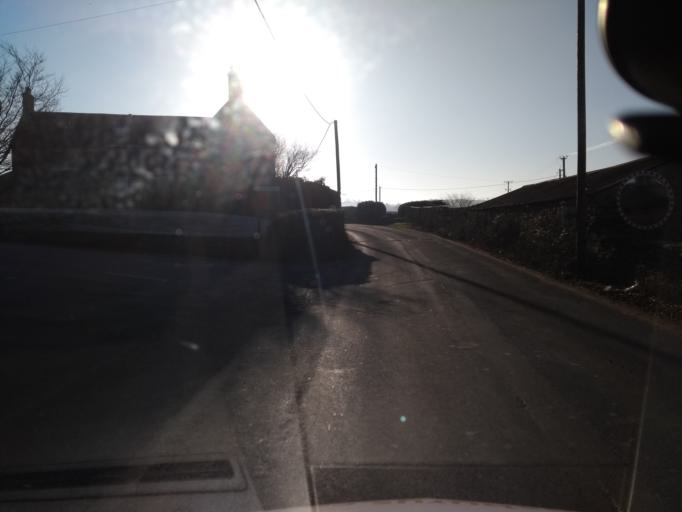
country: GB
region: England
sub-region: Somerset
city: Bruton
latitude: 51.1092
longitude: -2.4490
